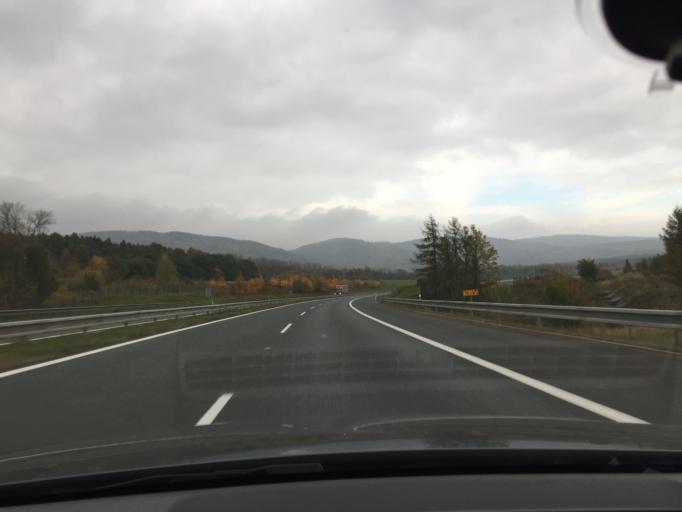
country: CZ
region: Ustecky
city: Chlumec
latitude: 50.7037
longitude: 13.9563
